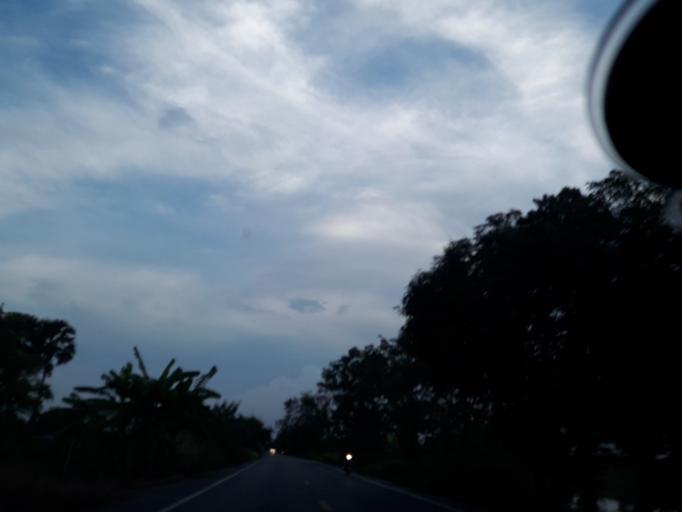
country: TH
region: Pathum Thani
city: Nong Suea
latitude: 14.1469
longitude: 100.8690
